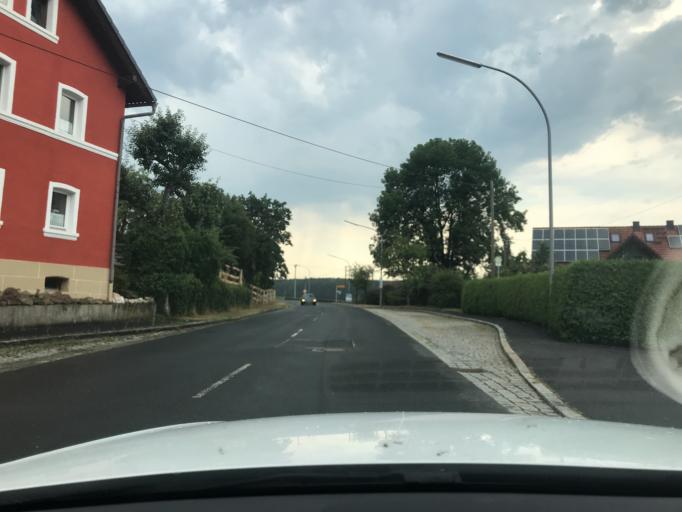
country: DE
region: Bavaria
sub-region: Upper Palatinate
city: Vorbach
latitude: 49.7924
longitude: 11.7660
